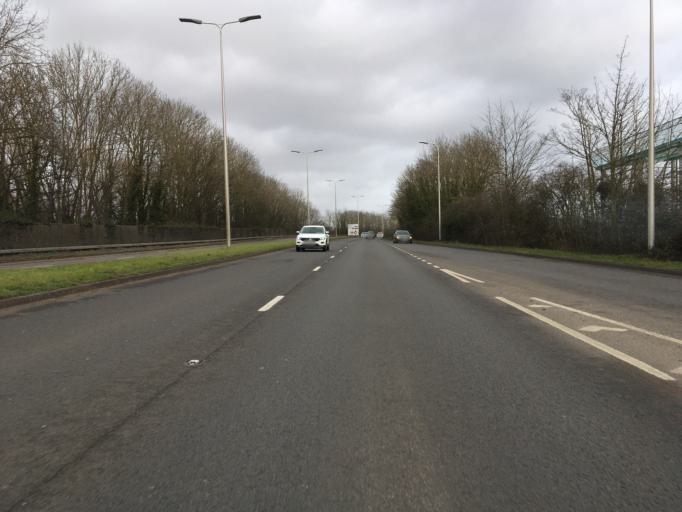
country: GB
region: England
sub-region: West Berkshire
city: Theale
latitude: 51.4344
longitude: -1.0784
